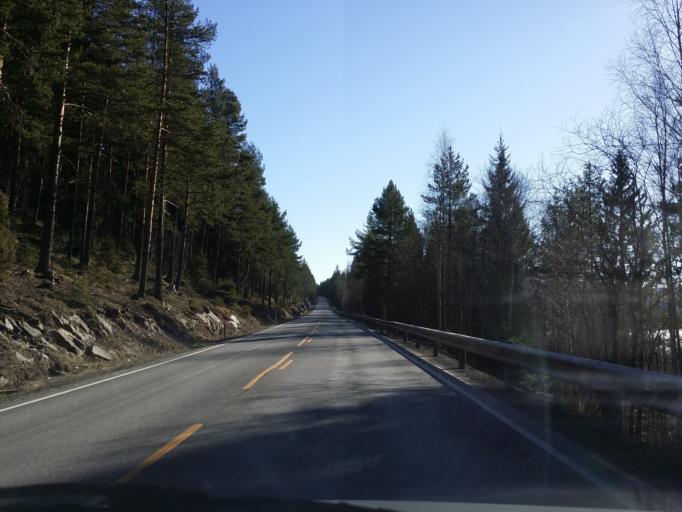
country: NO
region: Buskerud
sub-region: Ringerike
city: Honefoss
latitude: 60.2591
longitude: 10.1890
